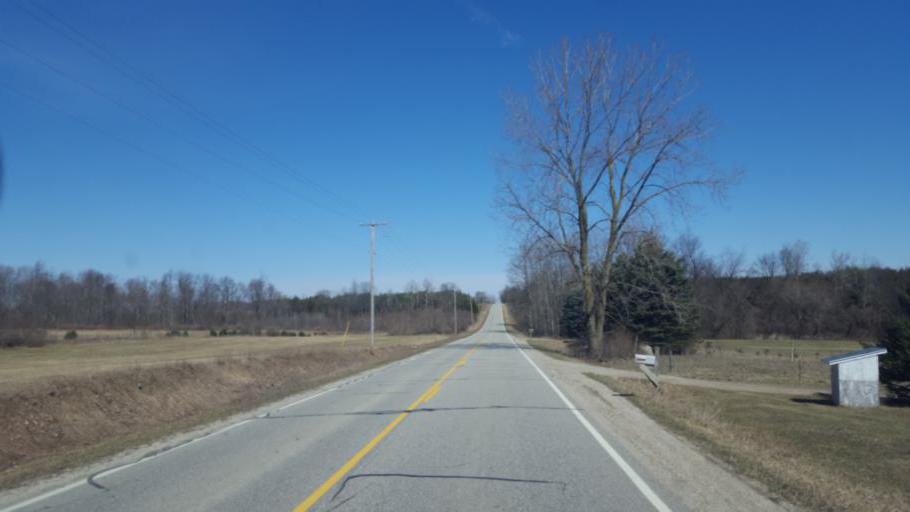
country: US
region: Michigan
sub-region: Montcalm County
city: Edmore
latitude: 43.4746
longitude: -85.0850
